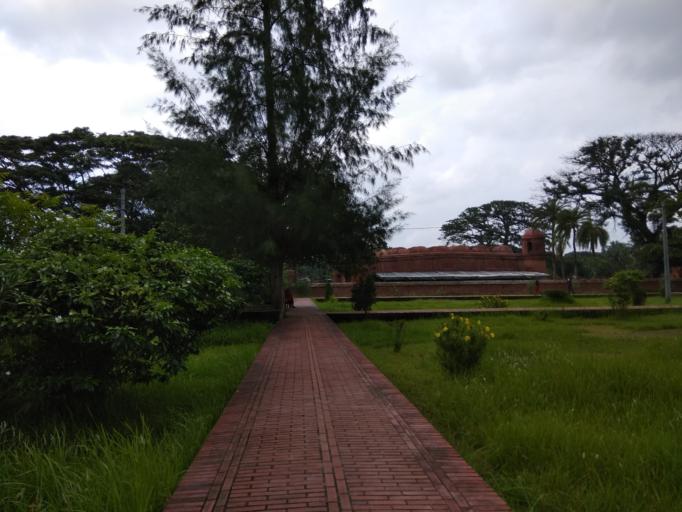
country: BD
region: Khulna
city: Khulna
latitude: 22.6734
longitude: 89.7414
